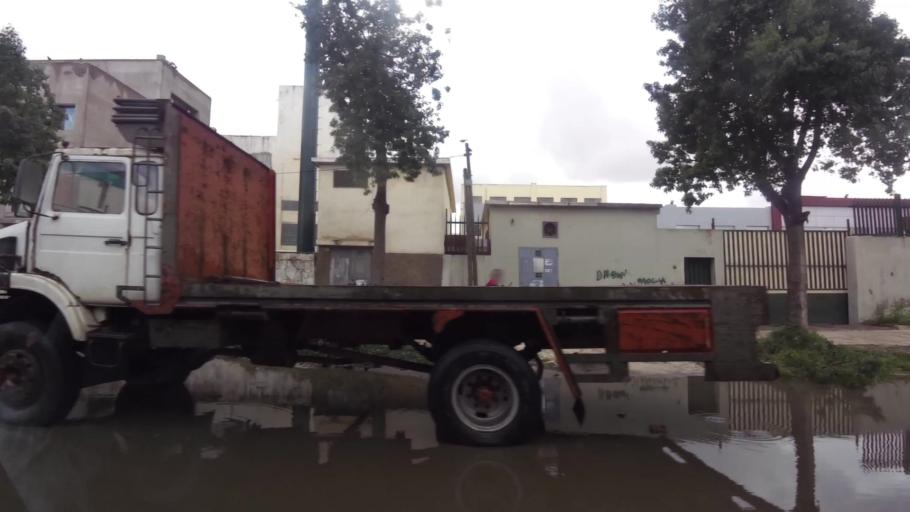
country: MA
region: Grand Casablanca
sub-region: Nouaceur
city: Bouskoura
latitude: 33.5132
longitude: -7.6559
